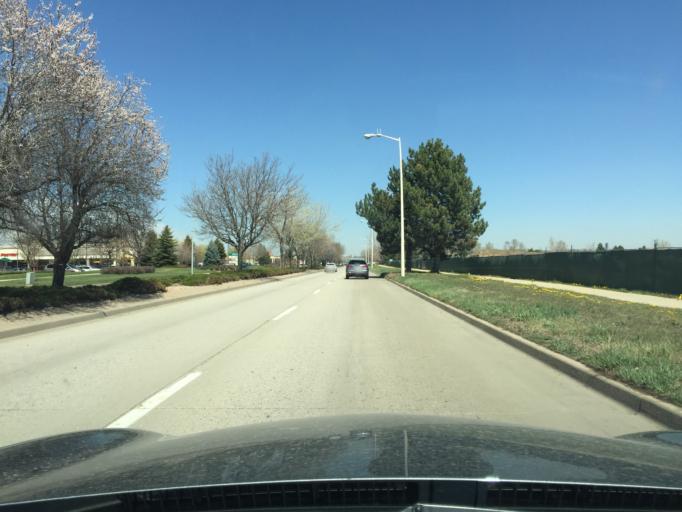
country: US
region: Colorado
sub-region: Boulder County
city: Longmont
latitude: 40.1466
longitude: -105.1307
